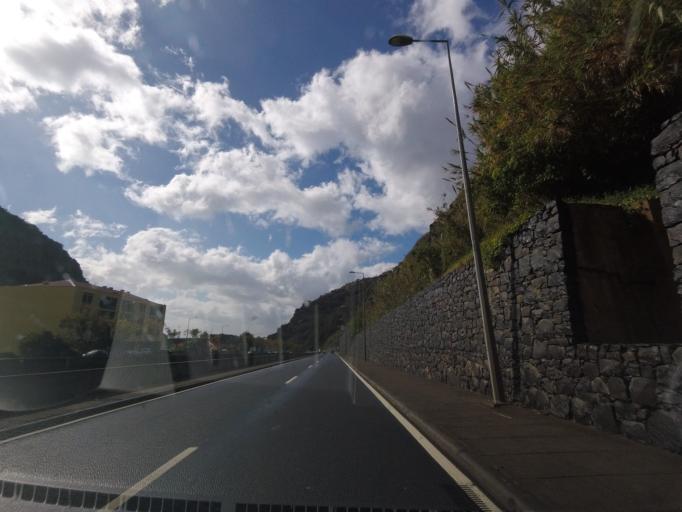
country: PT
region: Madeira
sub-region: Ribeira Brava
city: Campanario
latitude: 32.6789
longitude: -17.0610
